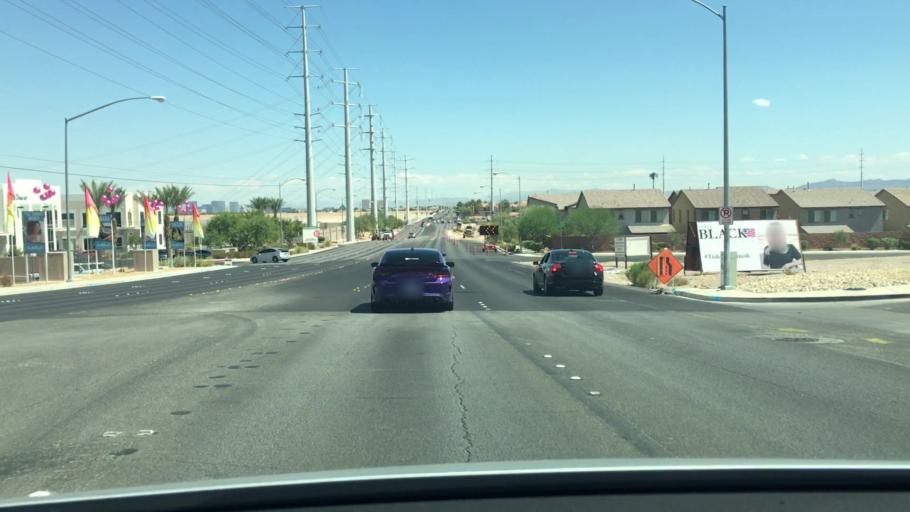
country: US
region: Nevada
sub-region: Clark County
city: Spring Valley
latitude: 36.0851
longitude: -115.2858
